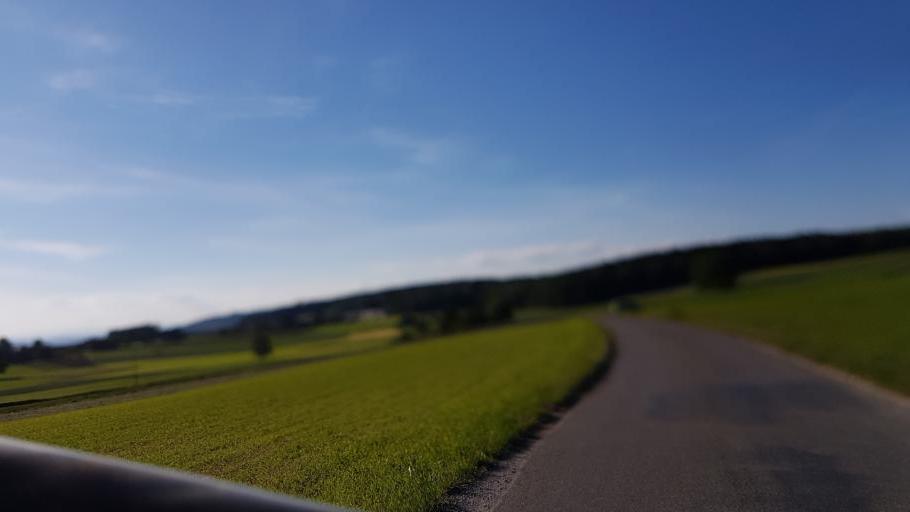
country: CH
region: Bern
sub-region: Bern-Mittelland District
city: Rubigen
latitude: 46.9050
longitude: 7.5680
